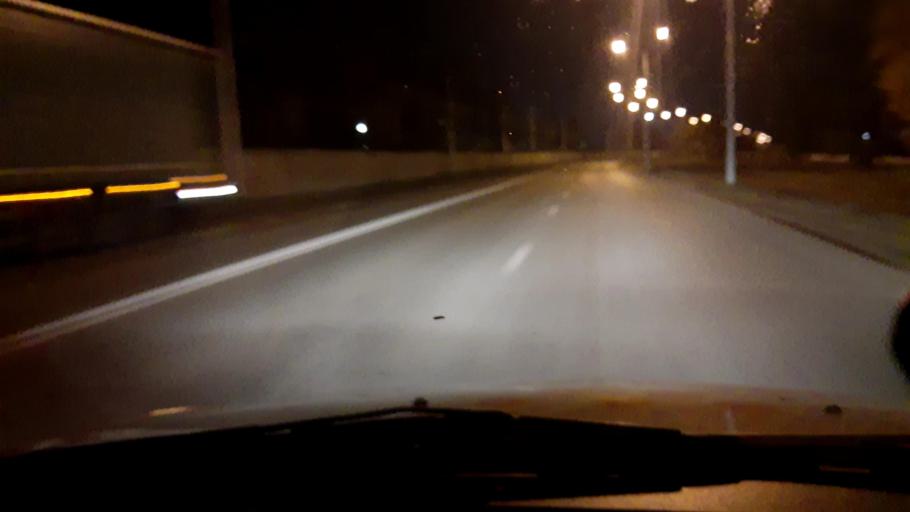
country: RU
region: Bashkortostan
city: Ufa
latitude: 54.8316
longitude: 56.0886
